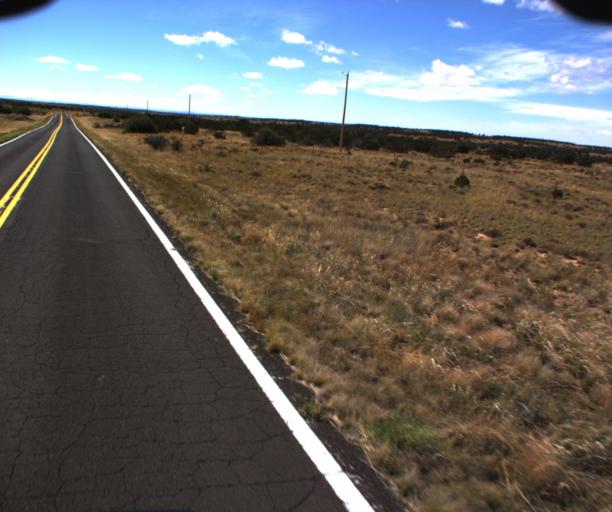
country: US
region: New Mexico
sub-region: McKinley County
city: Zuni Pueblo
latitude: 34.9598
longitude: -109.1574
